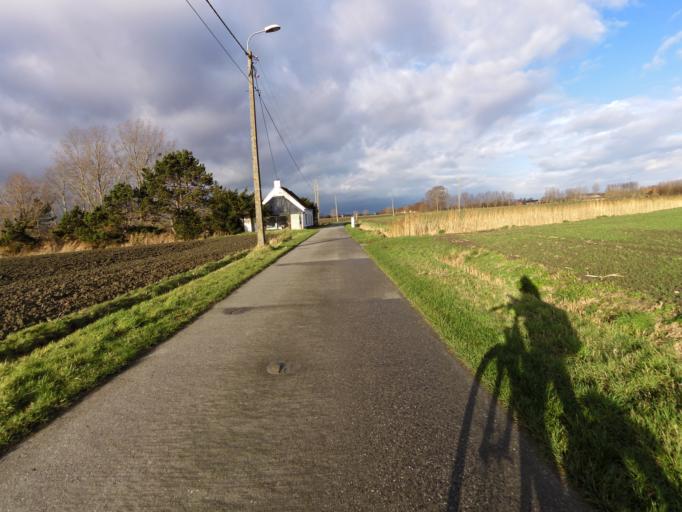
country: BE
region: Flanders
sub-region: Provincie West-Vlaanderen
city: Ostend
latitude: 51.1616
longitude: 2.8895
